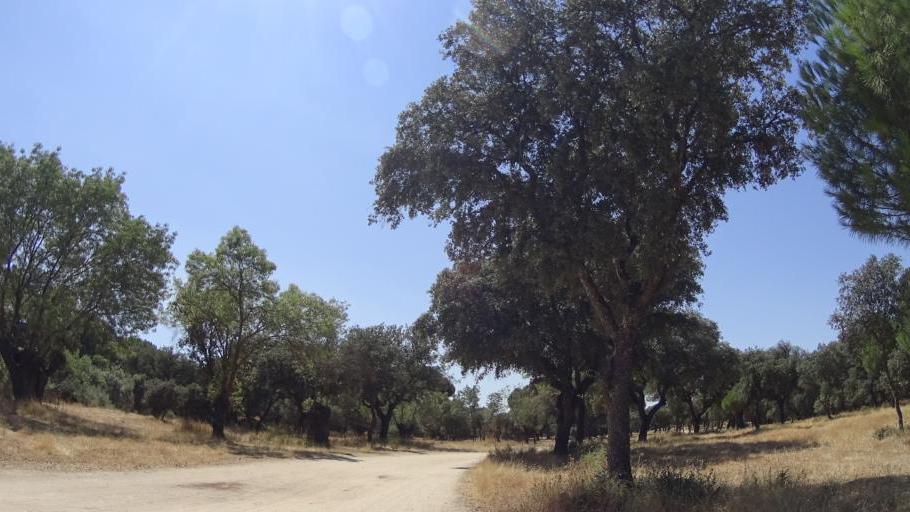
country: ES
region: Madrid
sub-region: Provincia de Madrid
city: Boadilla del Monte
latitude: 40.4216
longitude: -3.8557
